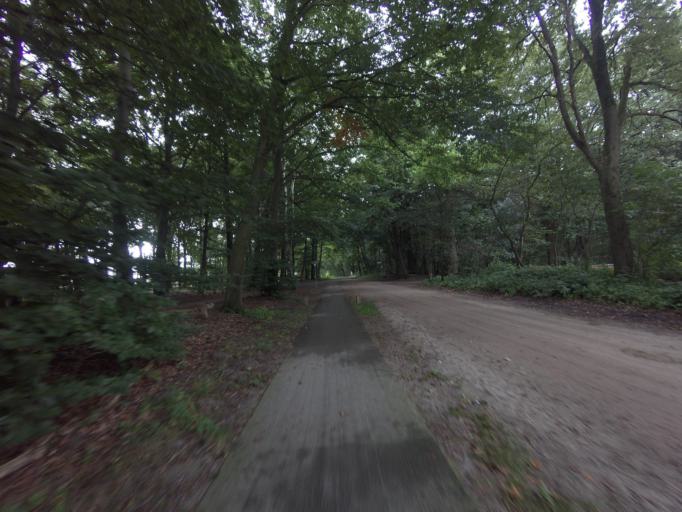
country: DE
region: Lower Saxony
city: Getelo
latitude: 52.4404
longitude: 6.8723
